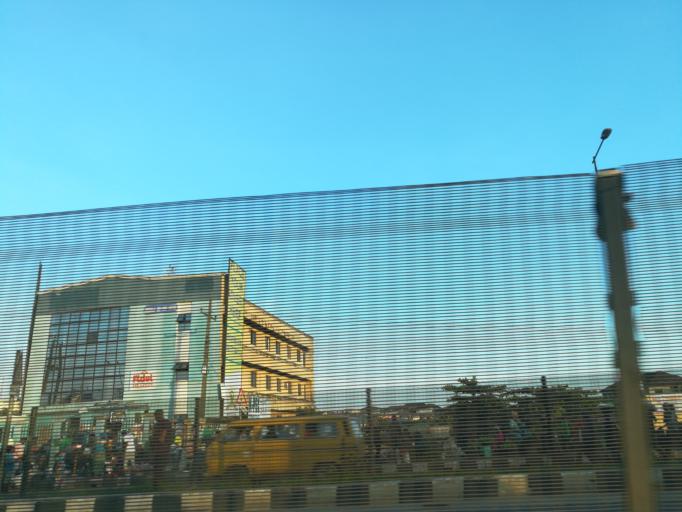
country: NG
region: Lagos
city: Ebute Ikorodu
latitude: 6.6250
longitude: 3.4837
